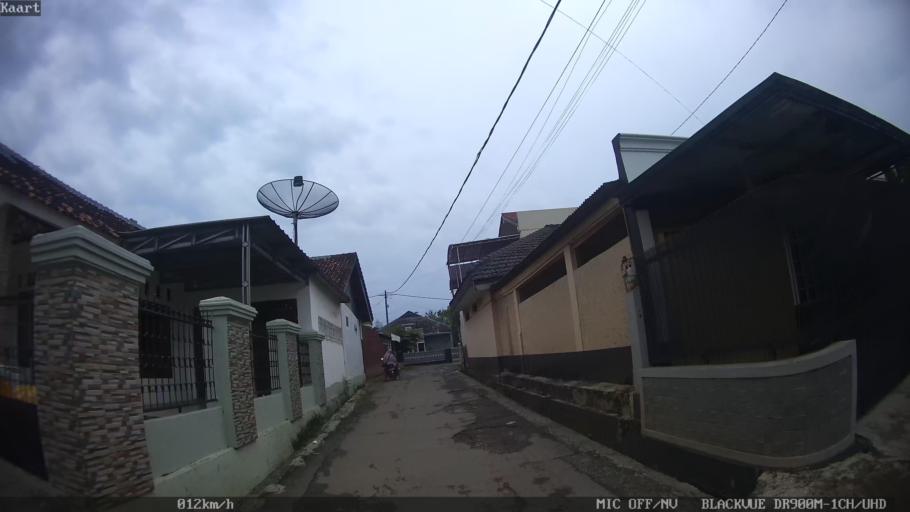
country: ID
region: Lampung
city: Kedaton
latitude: -5.3839
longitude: 105.2534
